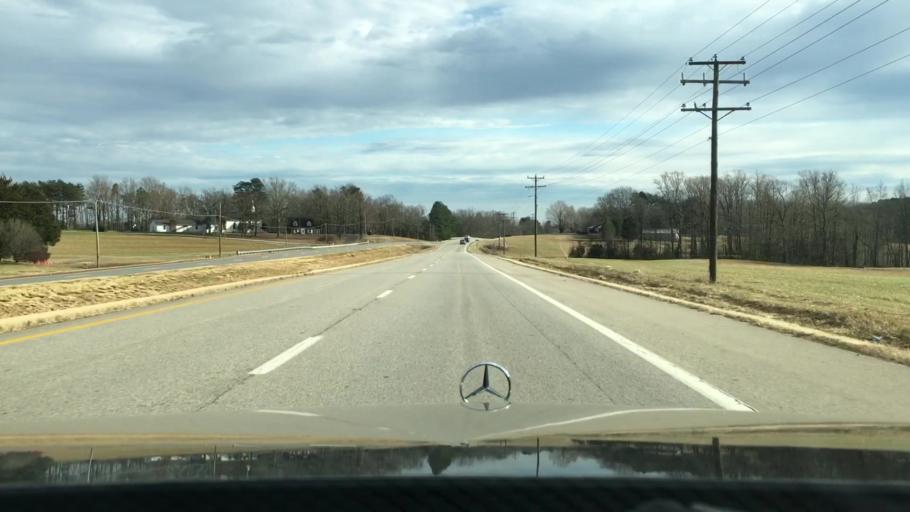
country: US
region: Virginia
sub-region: Pittsylvania County
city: Mount Hermon
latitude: 36.7204
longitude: -79.3836
